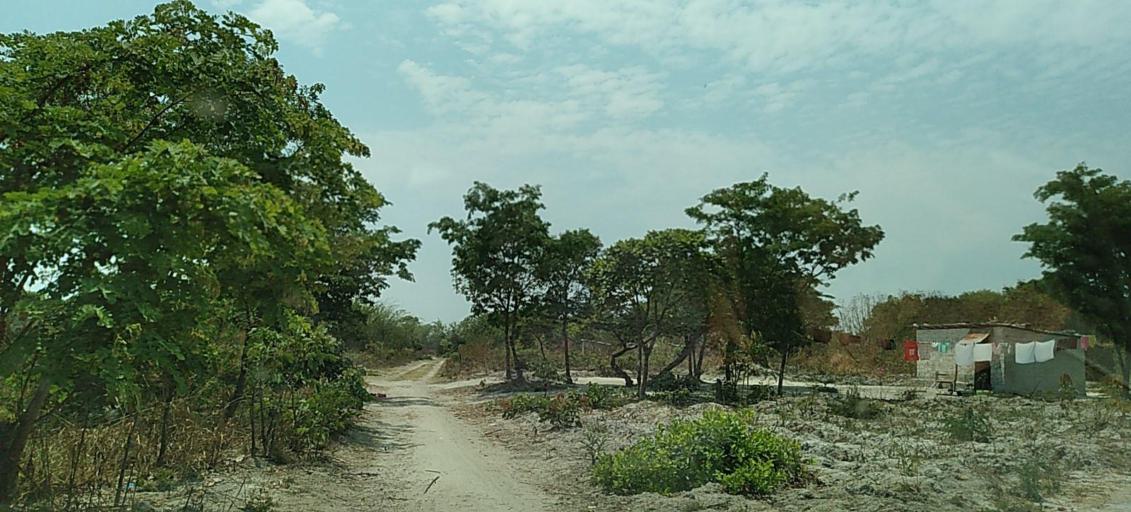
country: ZM
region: Copperbelt
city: Kalulushi
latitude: -12.9424
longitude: 28.1209
